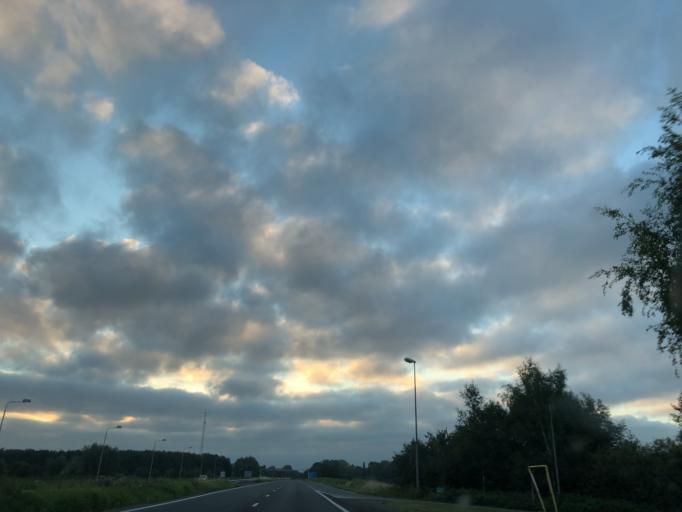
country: DE
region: Lower Saxony
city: Bunde
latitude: 53.1785
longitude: 7.2196
